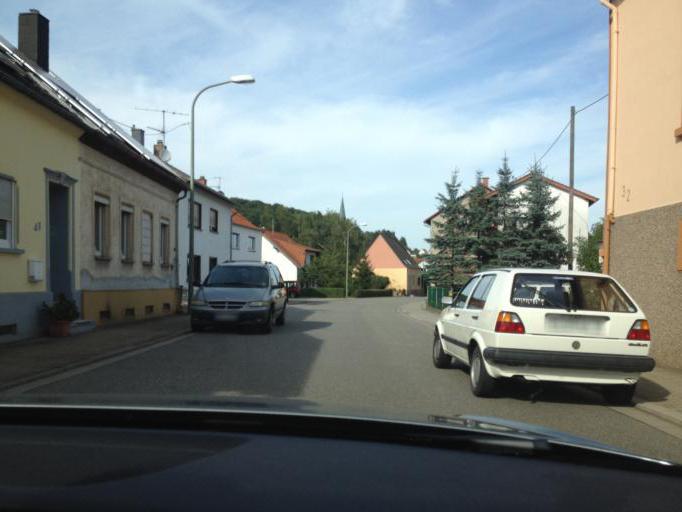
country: DE
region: Rheinland-Pfalz
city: Breitenbach
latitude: 49.4319
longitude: 7.2675
